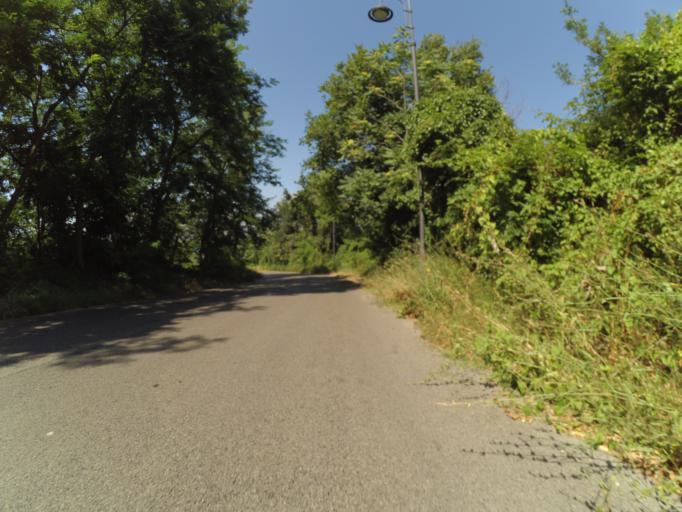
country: IT
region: Latium
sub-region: Provincia di Latina
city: Gaeta
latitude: 41.2116
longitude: 13.5732
